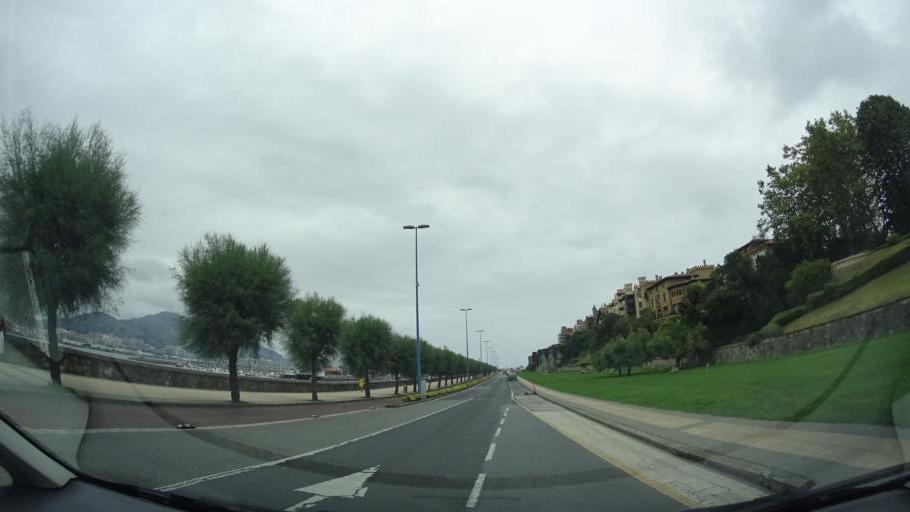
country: ES
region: Basque Country
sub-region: Bizkaia
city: Algorta
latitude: 43.3380
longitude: -3.0104
